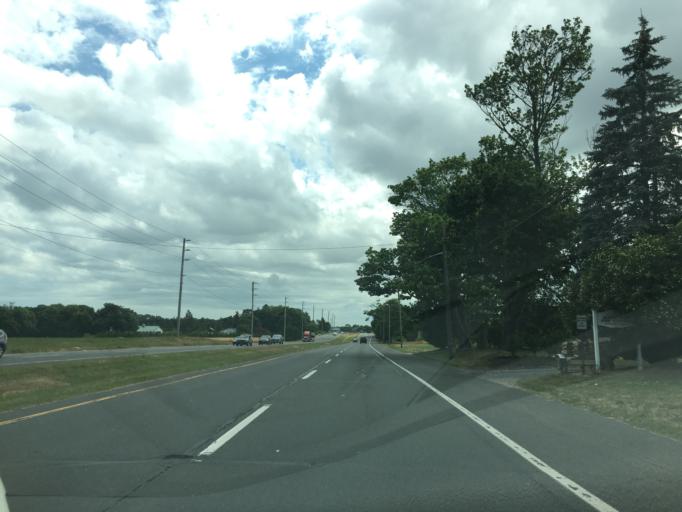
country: US
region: New York
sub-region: Suffolk County
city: Mattituck
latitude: 41.0128
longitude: -72.5152
